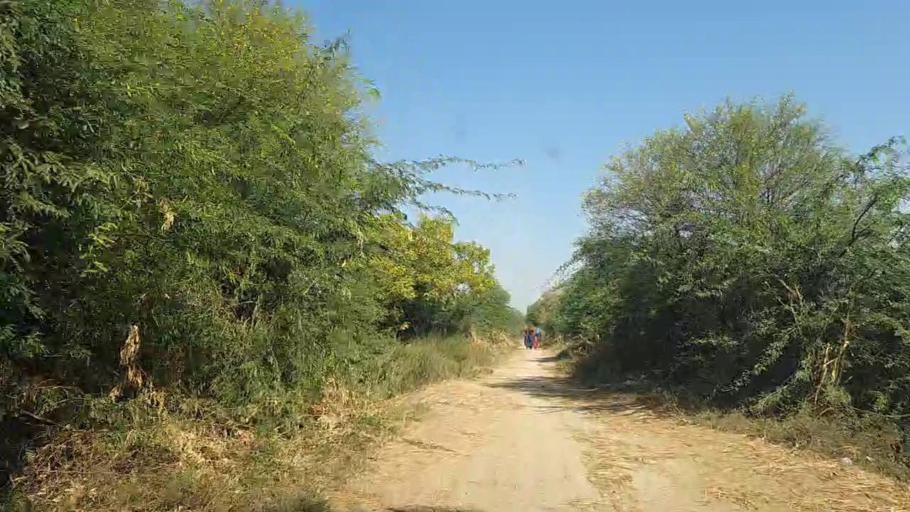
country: PK
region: Sindh
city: Thatta
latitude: 24.7847
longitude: 67.9733
